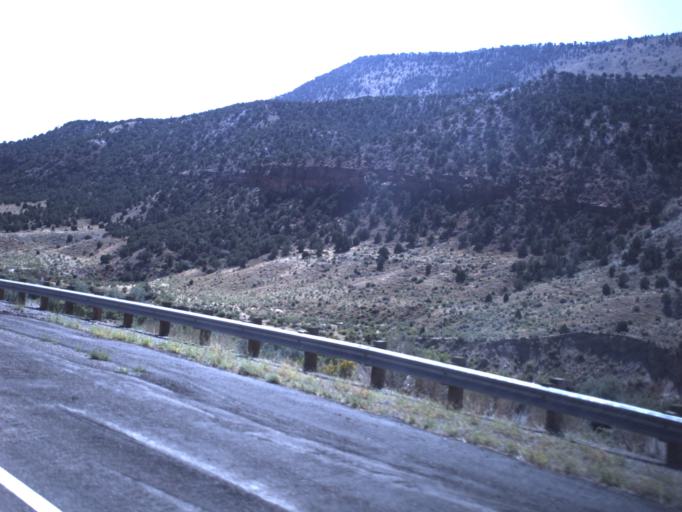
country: US
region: Utah
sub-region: Sevier County
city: Salina
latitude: 38.9256
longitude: -111.7796
